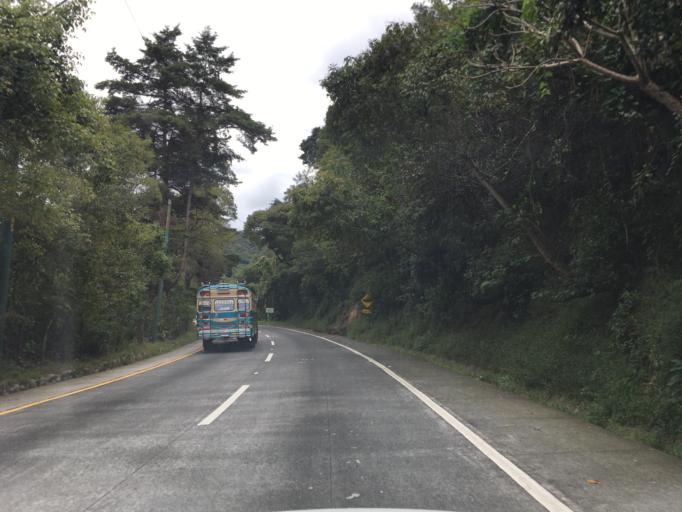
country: GT
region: Sacatepequez
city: Santa Lucia Milpas Altas
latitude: 14.5647
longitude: -90.6983
